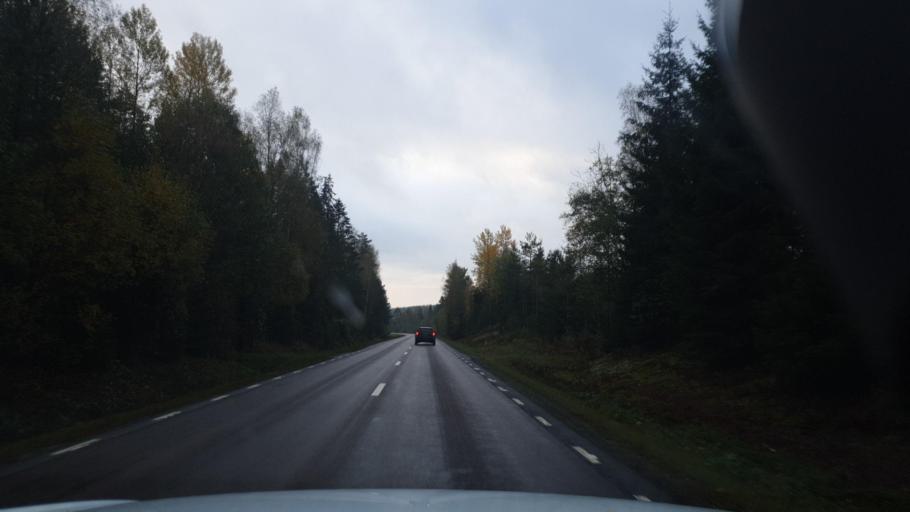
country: SE
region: Vaermland
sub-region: Arvika Kommun
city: Arvika
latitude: 59.6435
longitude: 12.7821
